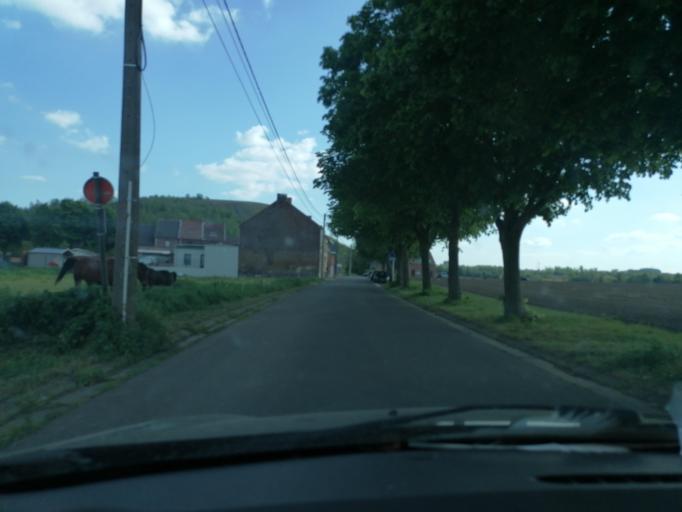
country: BE
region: Wallonia
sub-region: Province du Hainaut
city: Saint-Ghislain
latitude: 50.4290
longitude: 3.8178
